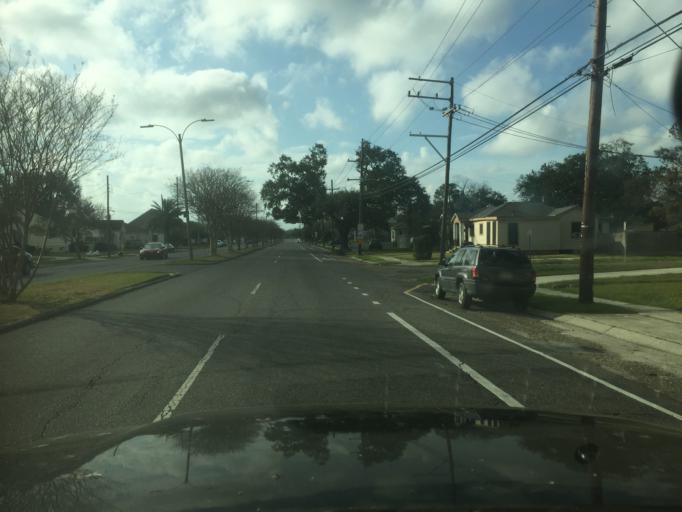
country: US
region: Louisiana
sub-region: Orleans Parish
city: New Orleans
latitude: 29.9890
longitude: -90.0820
